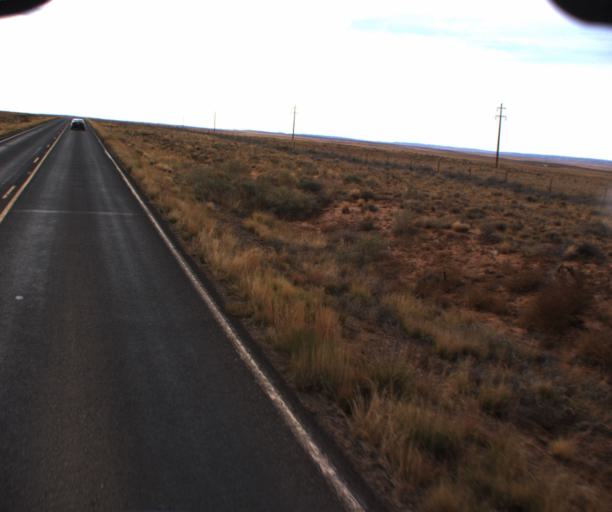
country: US
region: Arizona
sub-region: Apache County
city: Chinle
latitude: 35.9758
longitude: -109.5993
